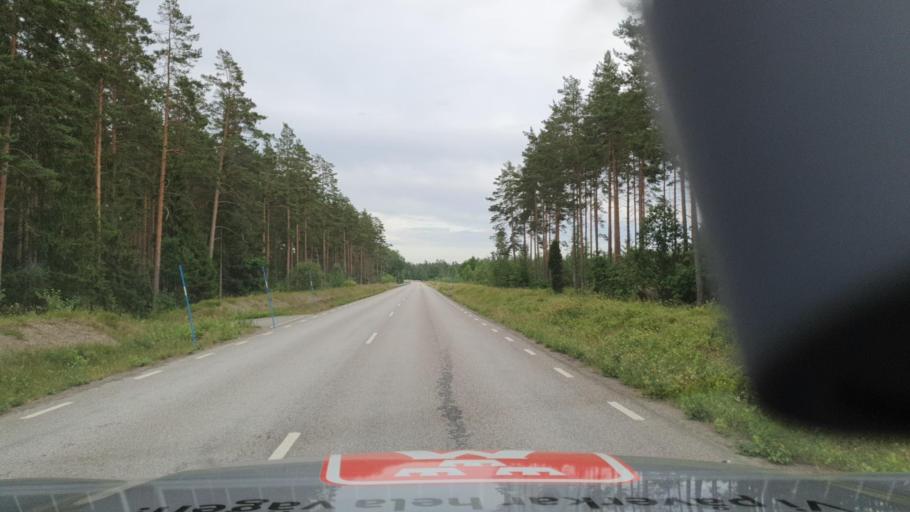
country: SE
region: Kalmar
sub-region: Nybro Kommun
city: Nybro
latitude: 56.6881
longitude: 15.9865
